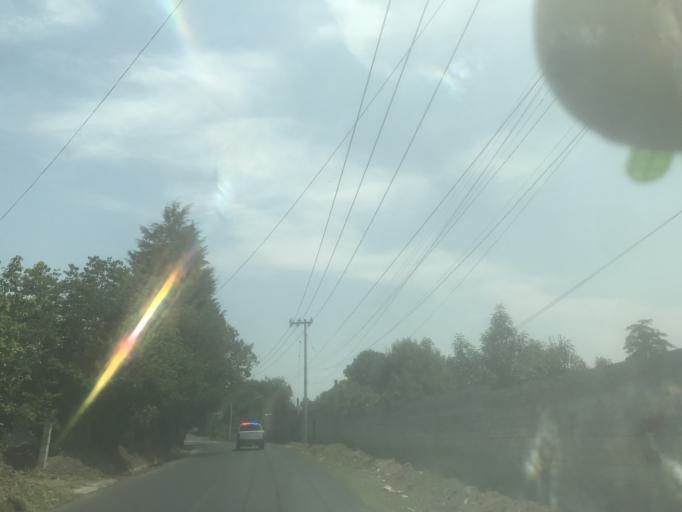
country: MX
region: Mexico
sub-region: Ozumba
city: San Jose Tlacotitlan
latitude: 18.9915
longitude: -98.8045
